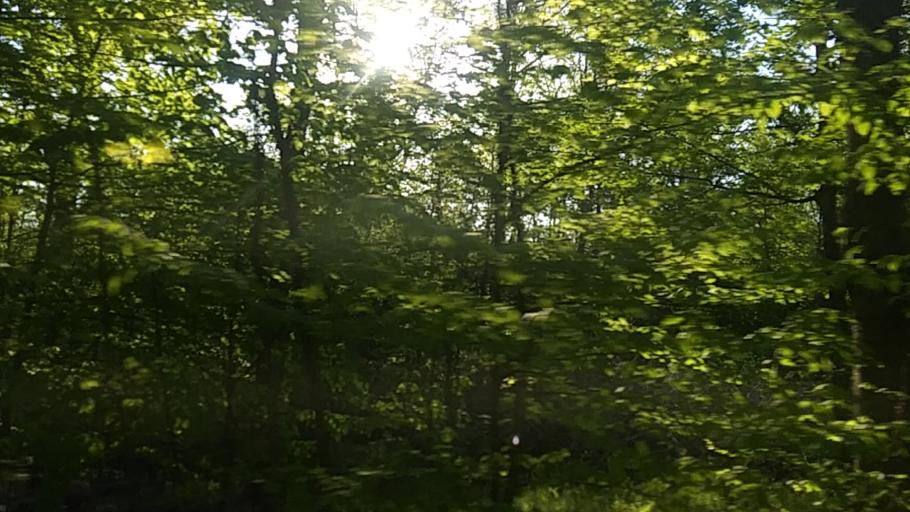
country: US
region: Massachusetts
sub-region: Franklin County
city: Shelburne Falls
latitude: 42.5846
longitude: -72.7444
